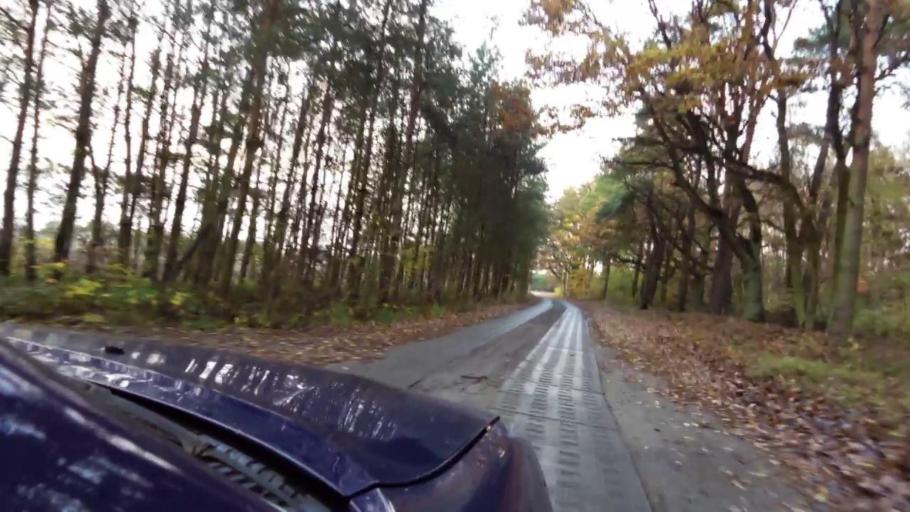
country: PL
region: West Pomeranian Voivodeship
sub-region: Powiat goleniowski
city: Goleniow
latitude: 53.5814
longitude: 14.7653
